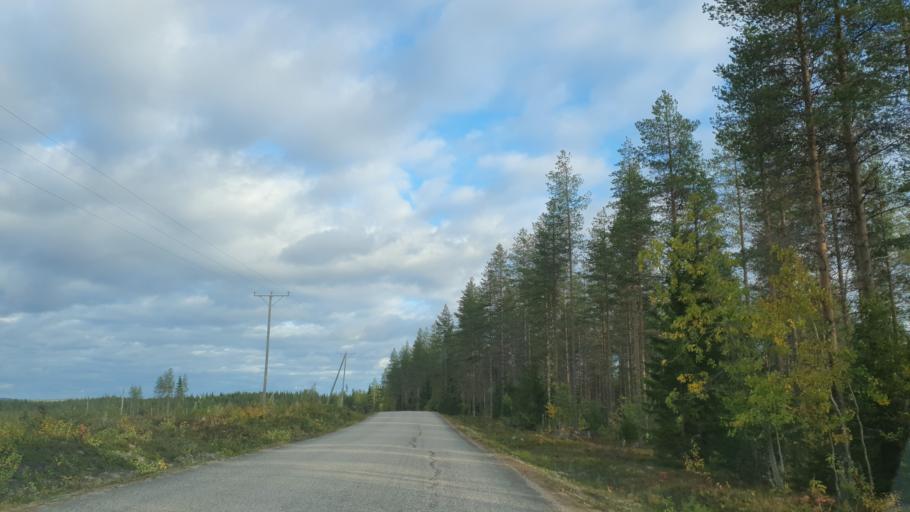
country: FI
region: North Karelia
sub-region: Pielisen Karjala
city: Lieksa
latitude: 63.9166
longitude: 30.1034
